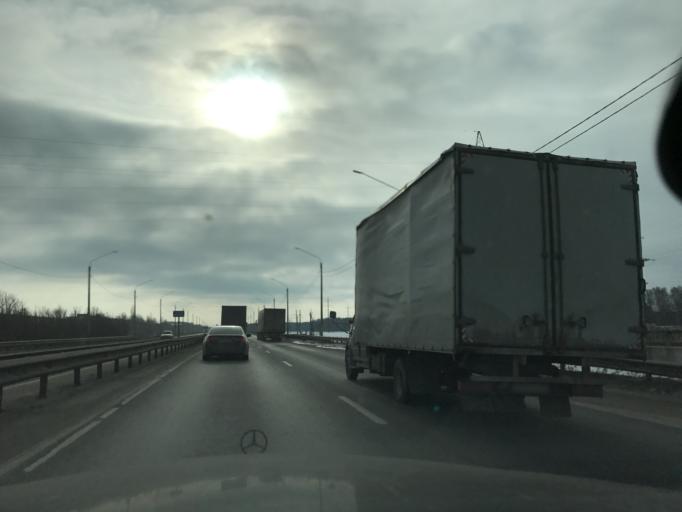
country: RU
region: Vladimir
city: Vyazniki
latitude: 56.2344
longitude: 42.1130
